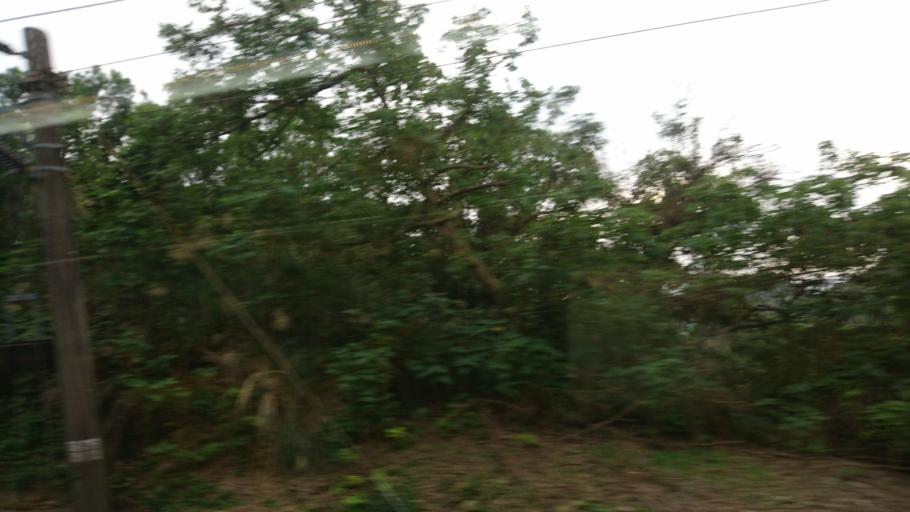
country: TW
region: Taiwan
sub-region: Hsinchu
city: Zhubei
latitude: 24.8604
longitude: 120.9964
